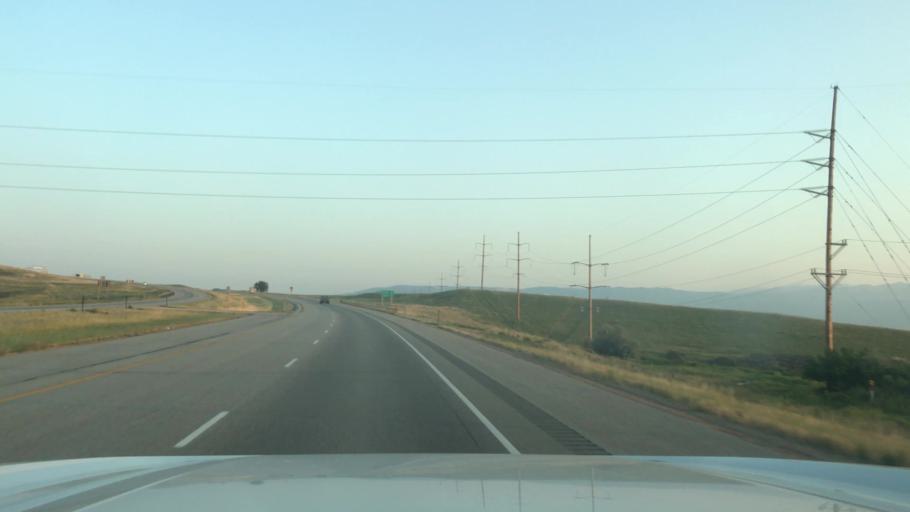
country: US
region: Wyoming
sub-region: Sheridan County
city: Sheridan
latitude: 44.7626
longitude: -106.9369
